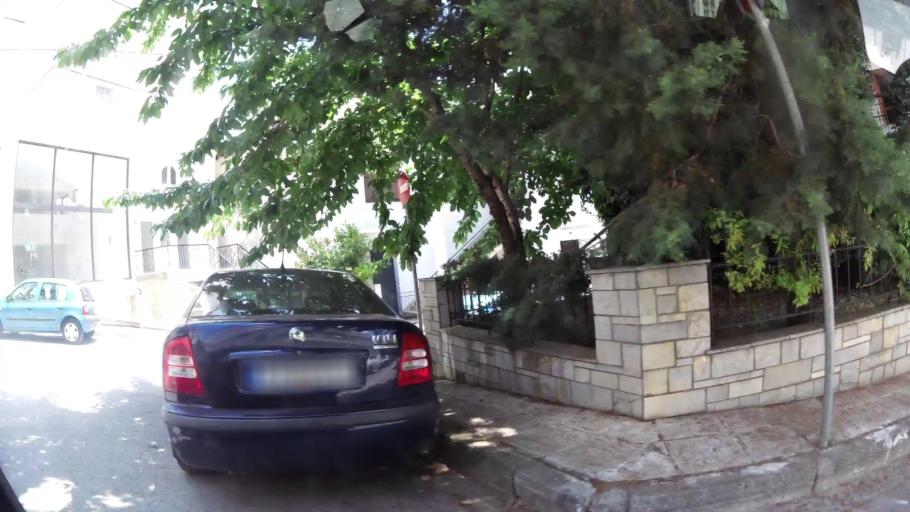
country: GR
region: West Macedonia
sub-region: Nomos Kozanis
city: Kozani
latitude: 40.3062
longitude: 21.7844
